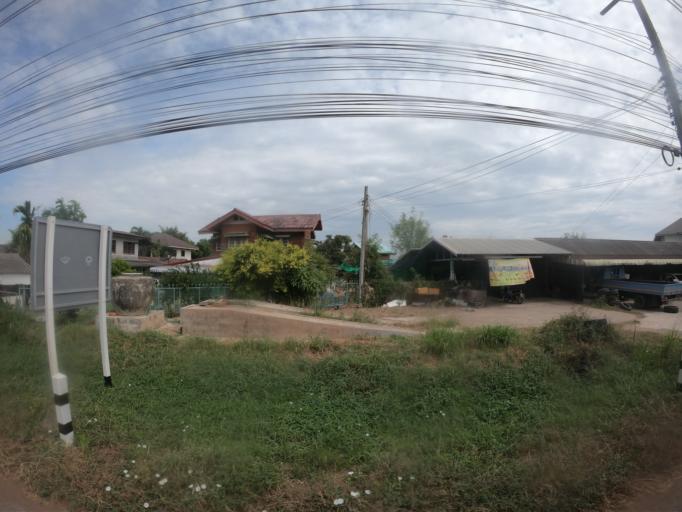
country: TH
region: Maha Sarakham
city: Chiang Yuen
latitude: 16.3472
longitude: 103.1228
